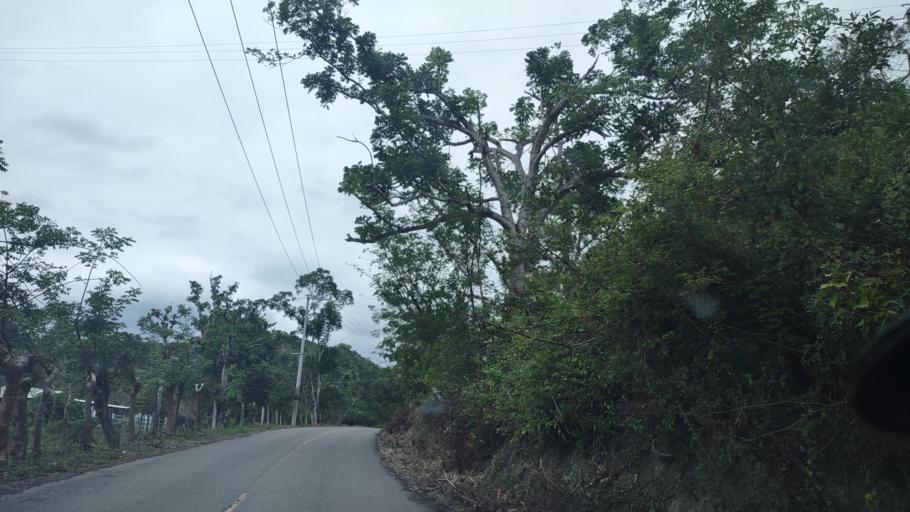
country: MX
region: Veracruz
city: Papantla de Olarte
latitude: 20.4449
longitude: -97.2948
